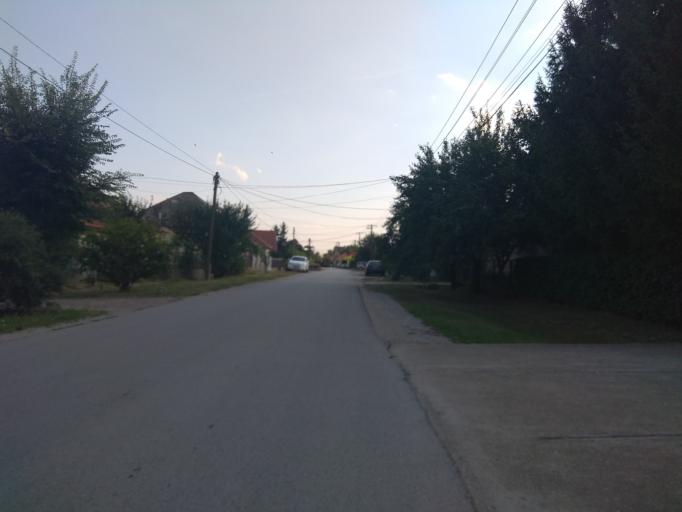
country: HU
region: Borsod-Abauj-Zemplen
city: Mezokeresztes
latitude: 47.8836
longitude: 20.6854
